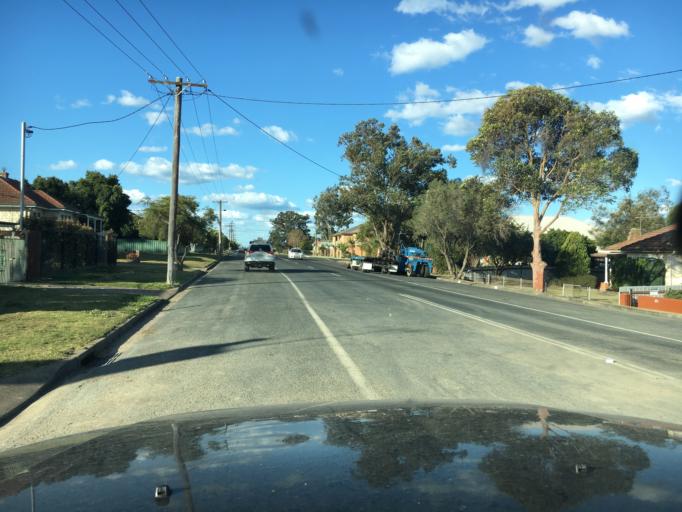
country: AU
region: New South Wales
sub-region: Maitland Municipality
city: East Maitland
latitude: -32.7573
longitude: 151.5838
